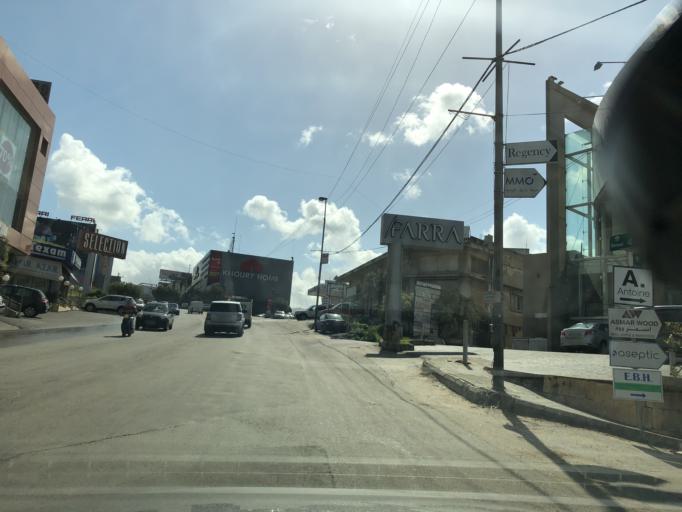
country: LB
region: Mont-Liban
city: Baabda
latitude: 33.8641
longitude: 35.5469
